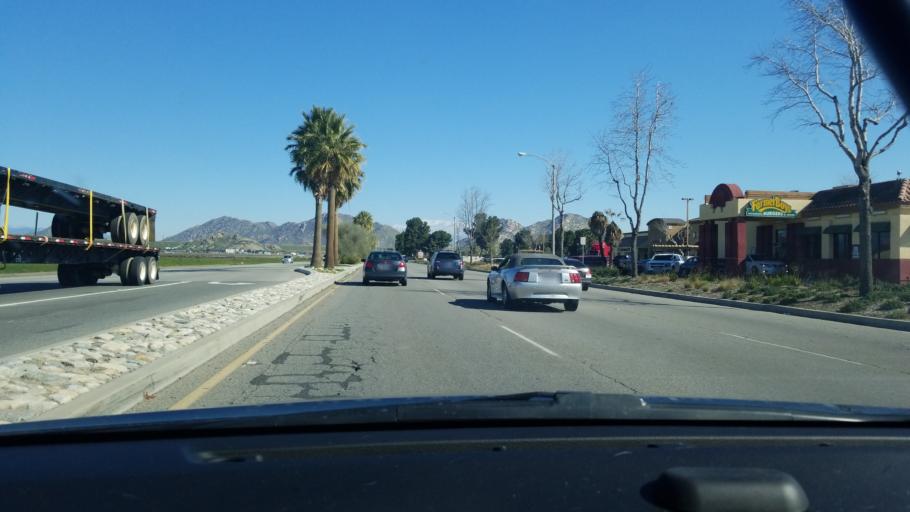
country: US
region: California
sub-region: Riverside County
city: March Air Force Base
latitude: 33.8445
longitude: -117.2235
